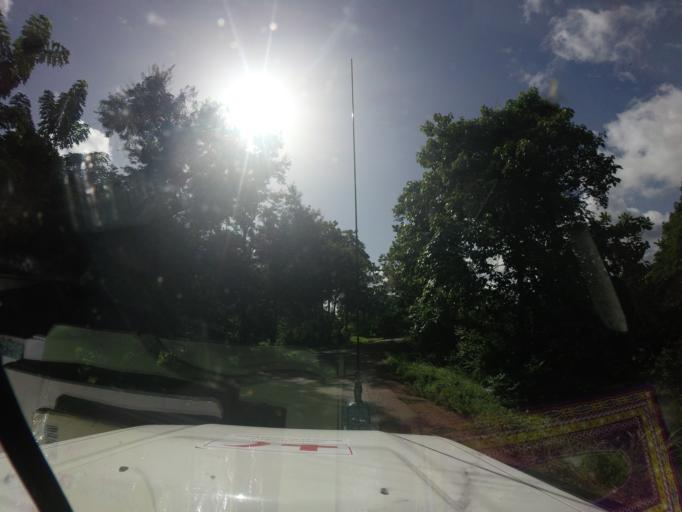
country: GN
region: Mamou
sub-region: Mamou Prefecture
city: Mamou
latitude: 10.3114
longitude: -12.2336
